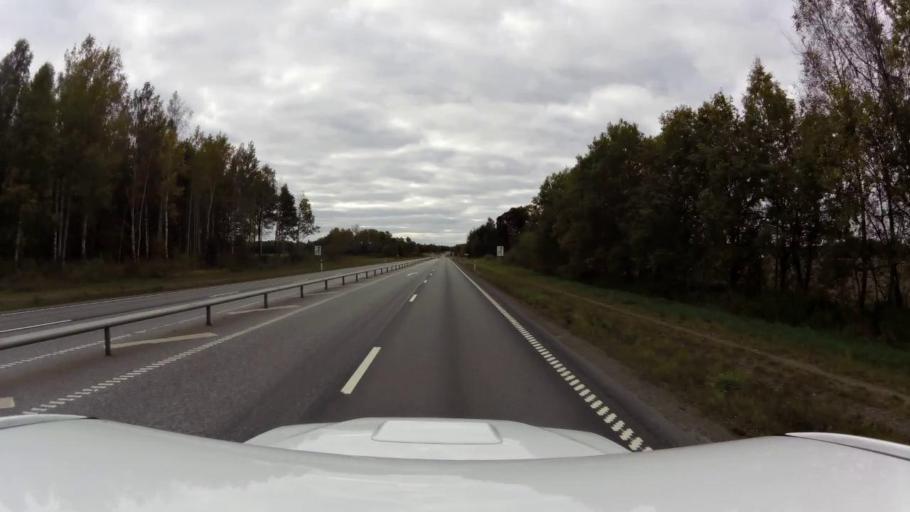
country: SE
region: OEstergoetland
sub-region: Linkopings Kommun
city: Malmslatt
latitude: 58.3733
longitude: 15.5433
